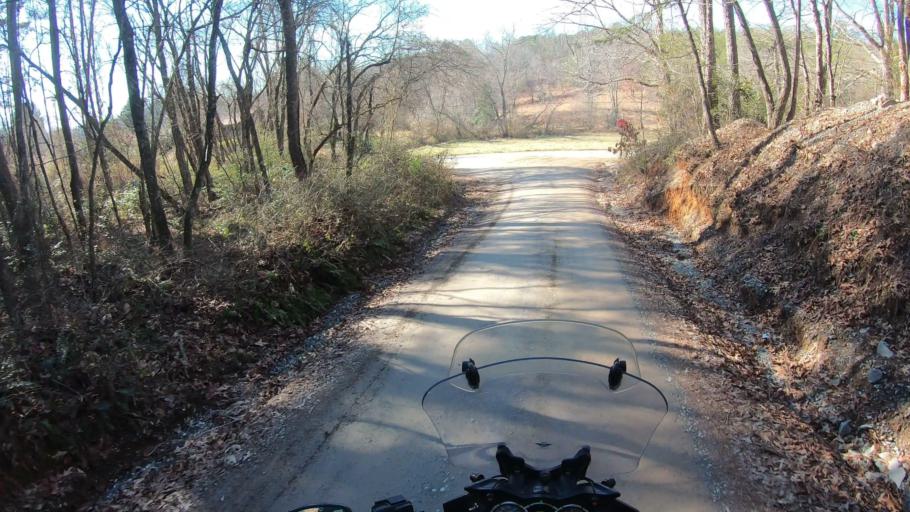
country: US
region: Georgia
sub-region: Fannin County
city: McCaysville
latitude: 34.9866
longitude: -84.3320
